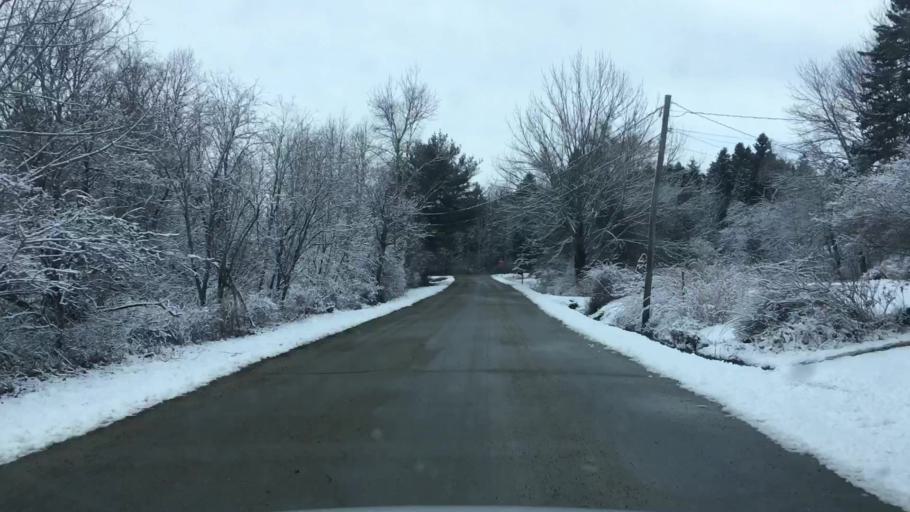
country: US
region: Maine
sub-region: Knox County
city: Owls Head
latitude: 44.0690
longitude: -69.0730
